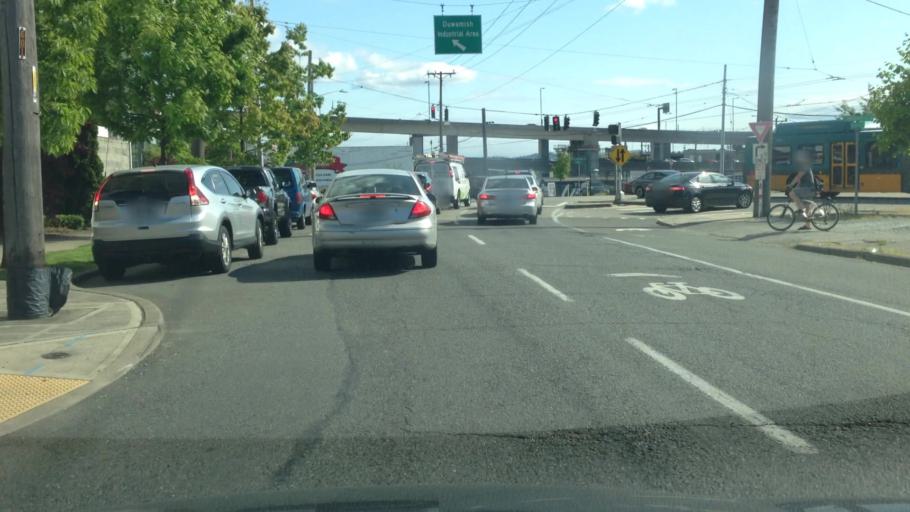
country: US
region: Washington
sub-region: King County
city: Seattle
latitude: 47.5950
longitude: -122.3250
